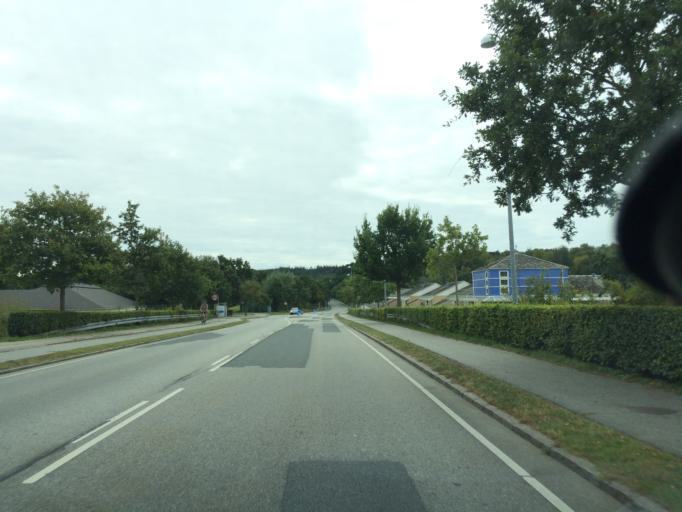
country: DK
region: South Denmark
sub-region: Aabenraa Kommune
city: Aabenraa
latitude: 55.0305
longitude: 9.4089
